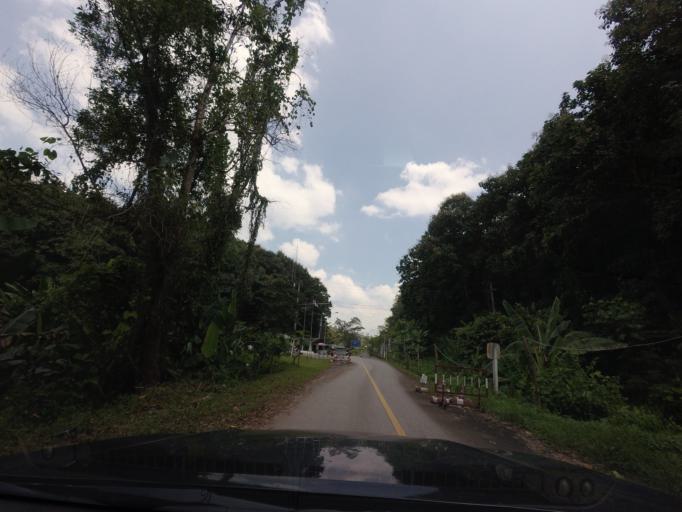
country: TH
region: Loei
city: Na Haeo
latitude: 17.6397
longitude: 100.9066
